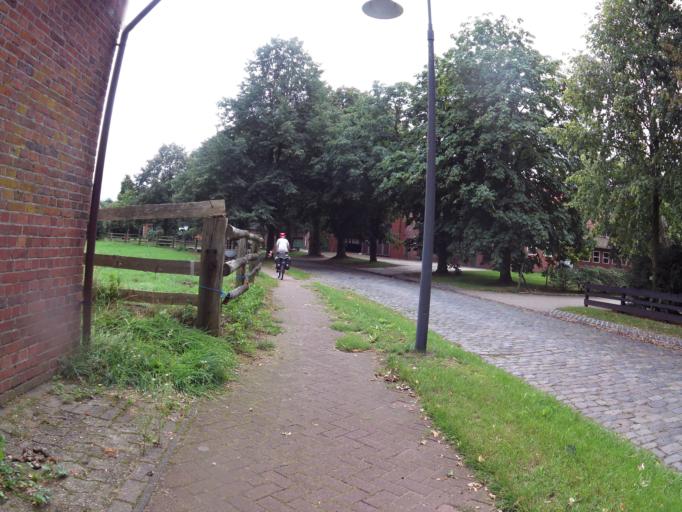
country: DE
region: Lower Saxony
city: Lunestedt
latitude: 53.4935
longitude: 8.7160
